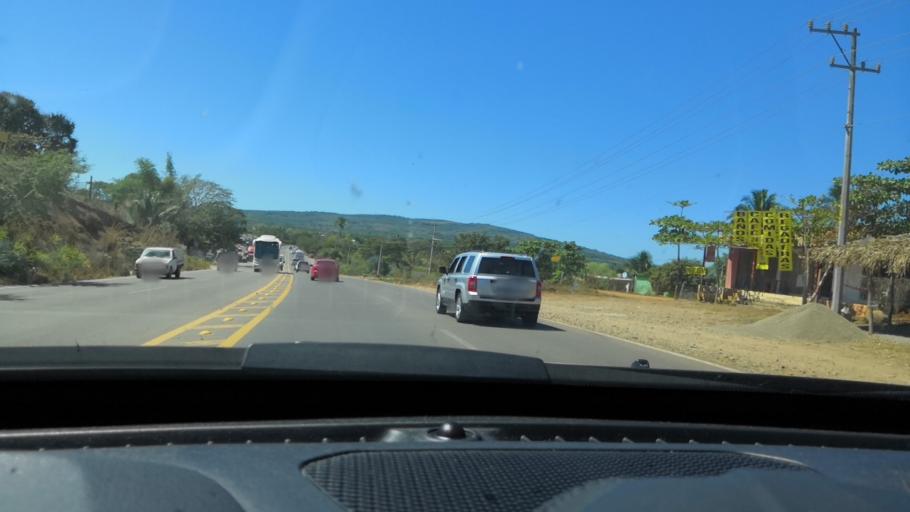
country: MX
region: Nayarit
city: Las Varas
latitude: 21.1753
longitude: -105.1438
